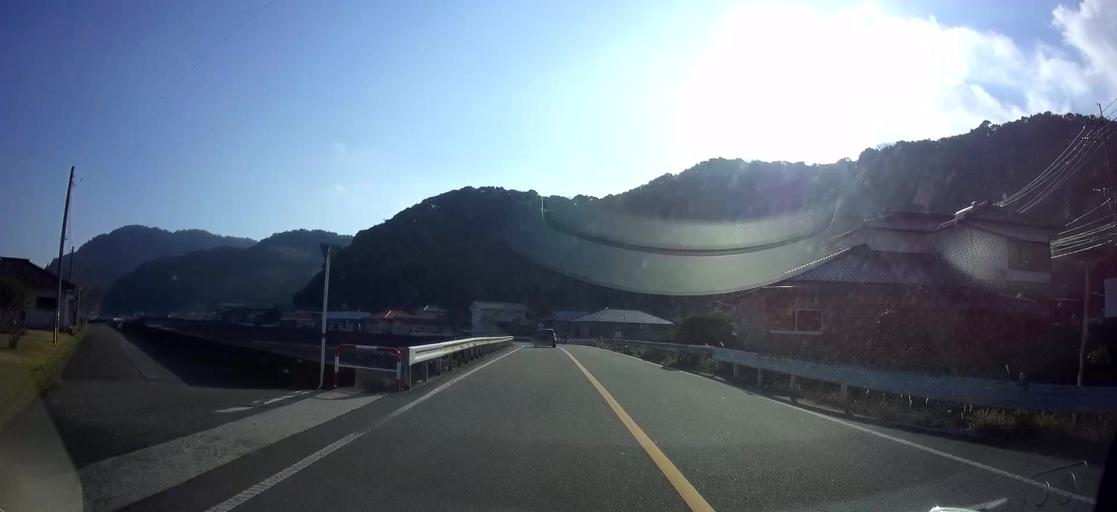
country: JP
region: Kumamoto
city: Hondo
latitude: 32.4275
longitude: 130.4023
